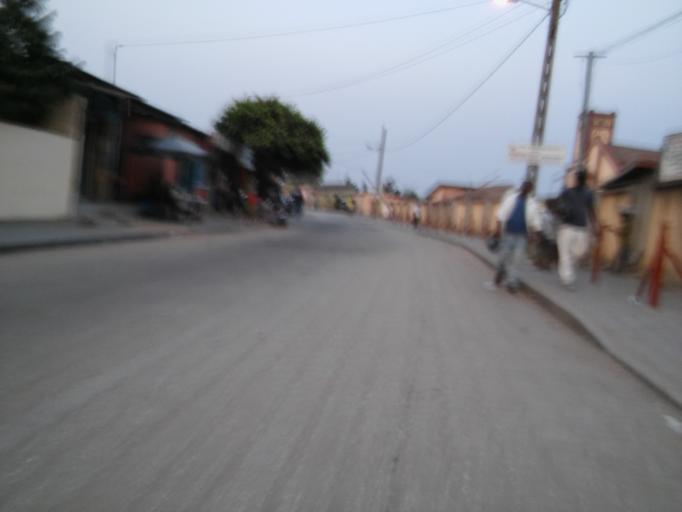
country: BJ
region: Atlantique
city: Abomey-Calavi
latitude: 6.3897
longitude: 2.3462
